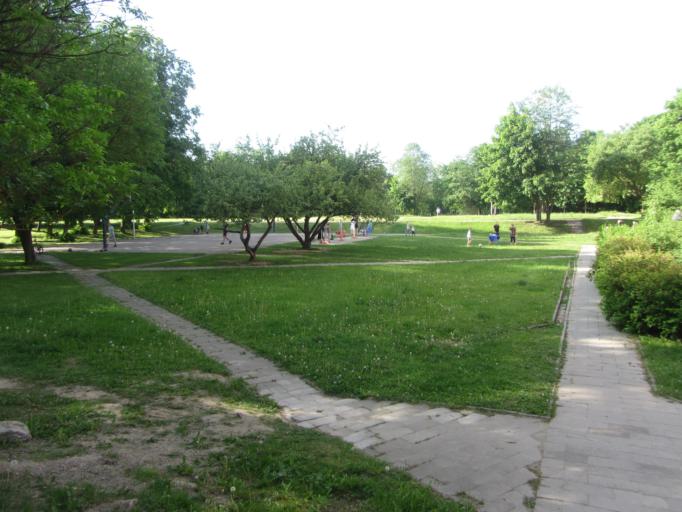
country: LT
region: Vilnius County
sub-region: Vilnius
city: Fabijoniskes
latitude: 54.7450
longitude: 25.2766
